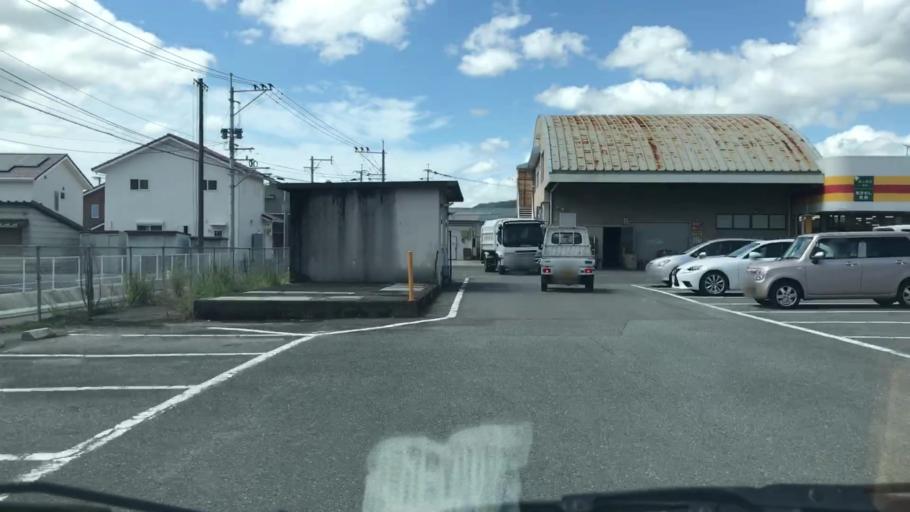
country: JP
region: Saga Prefecture
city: Takeocho-takeo
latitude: 33.2195
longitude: 130.0681
